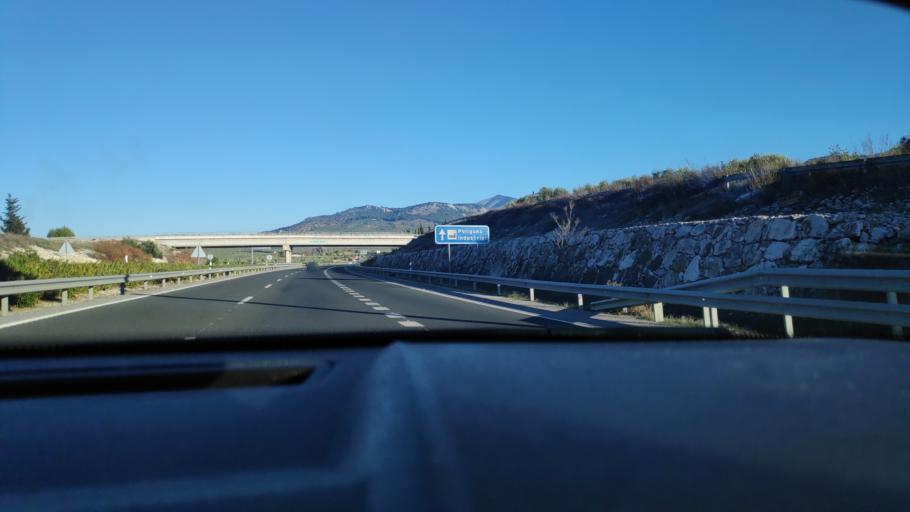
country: ES
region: Andalusia
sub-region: Provincia de Jaen
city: Torredonjimeno
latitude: 37.7532
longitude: -3.9482
